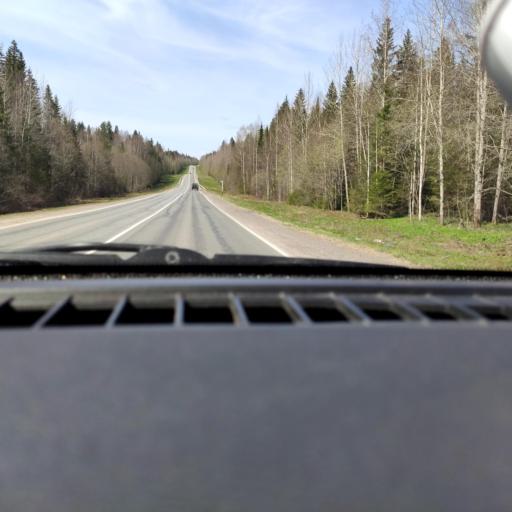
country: RU
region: Perm
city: Perm
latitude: 58.1605
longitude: 56.2459
